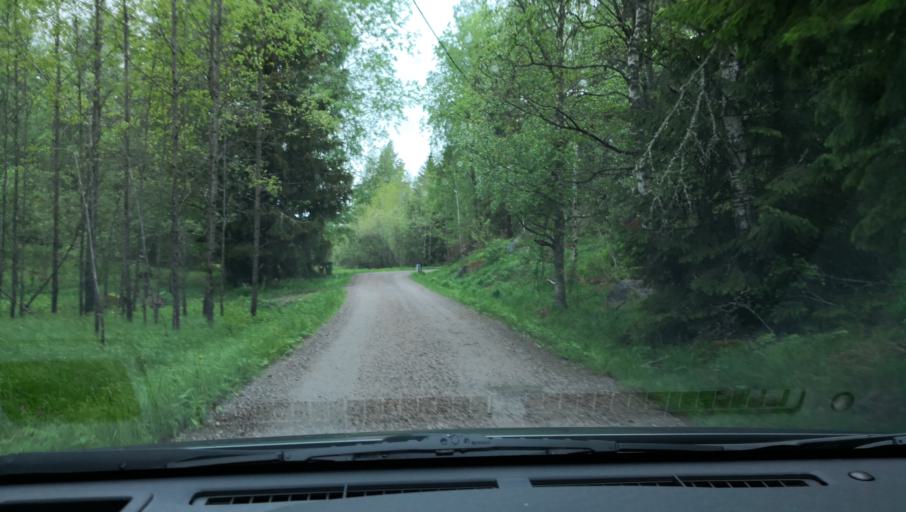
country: SE
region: Uppsala
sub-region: Heby Kommun
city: OEstervala
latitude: 59.9929
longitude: 17.2504
